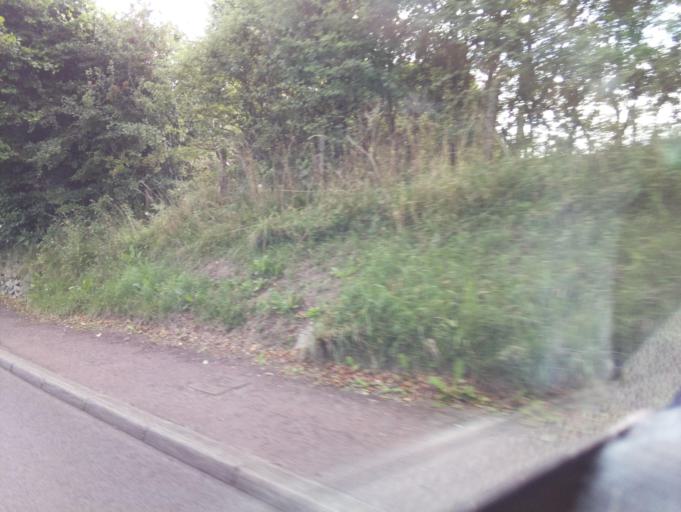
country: GB
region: Scotland
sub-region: The Scottish Borders
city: West Linton
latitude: 55.7585
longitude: -3.3501
